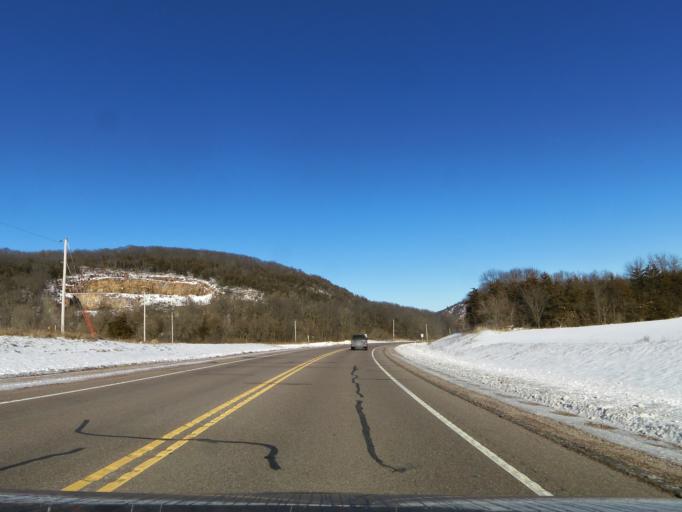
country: US
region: Wisconsin
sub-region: Sauk County
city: Baraboo
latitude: 43.4878
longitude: -89.6401
